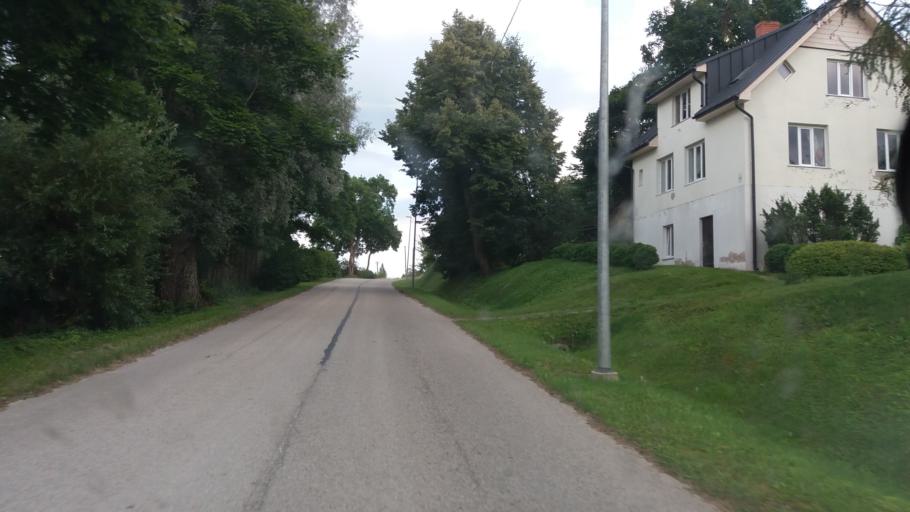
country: LV
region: Talsu Rajons
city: Sabile
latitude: 57.0384
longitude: 22.5707
